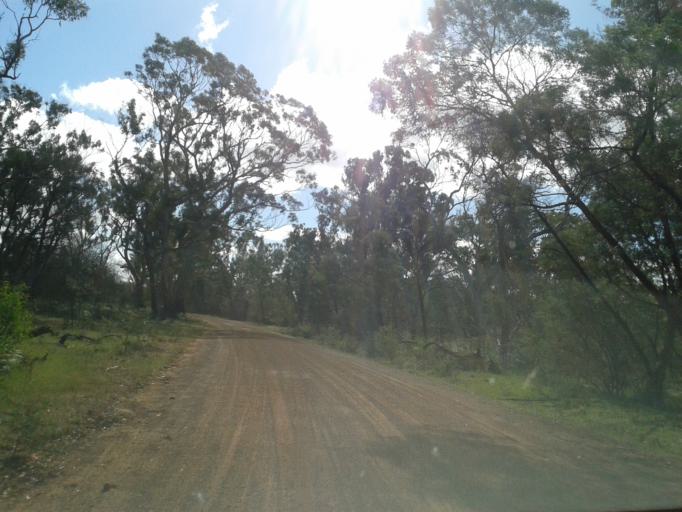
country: AU
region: Victoria
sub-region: Horsham
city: Horsham
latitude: -37.2406
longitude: 142.2470
